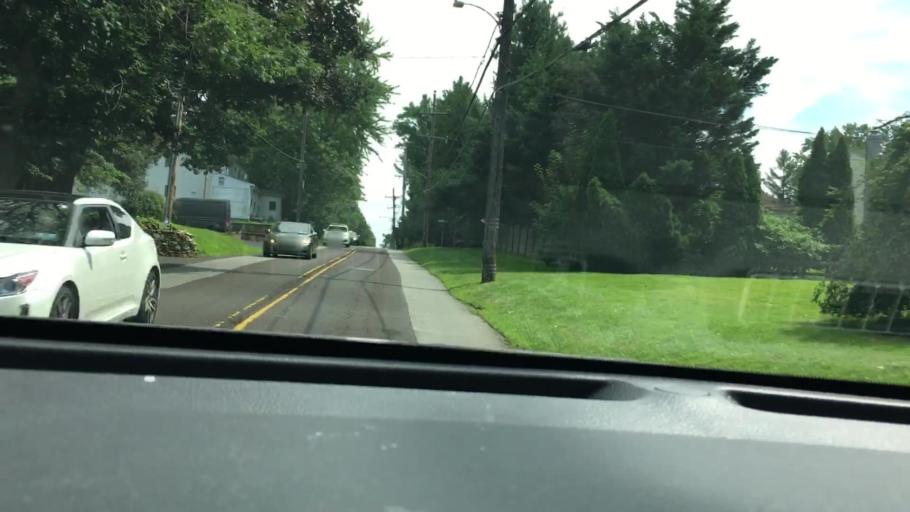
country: US
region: Pennsylvania
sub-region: Montgomery County
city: Bryn Athyn
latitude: 40.1360
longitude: -75.0363
